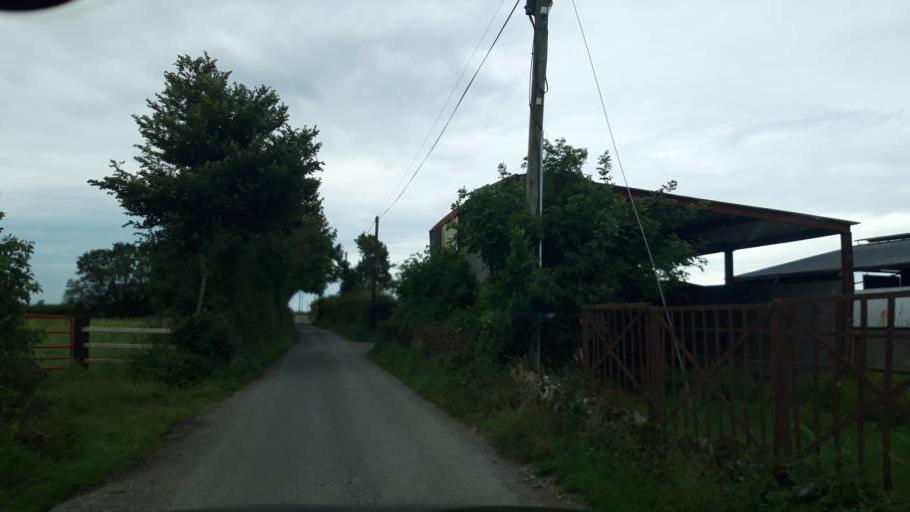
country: IE
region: Leinster
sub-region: Kilkenny
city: Ballyragget
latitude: 52.7926
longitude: -7.3329
